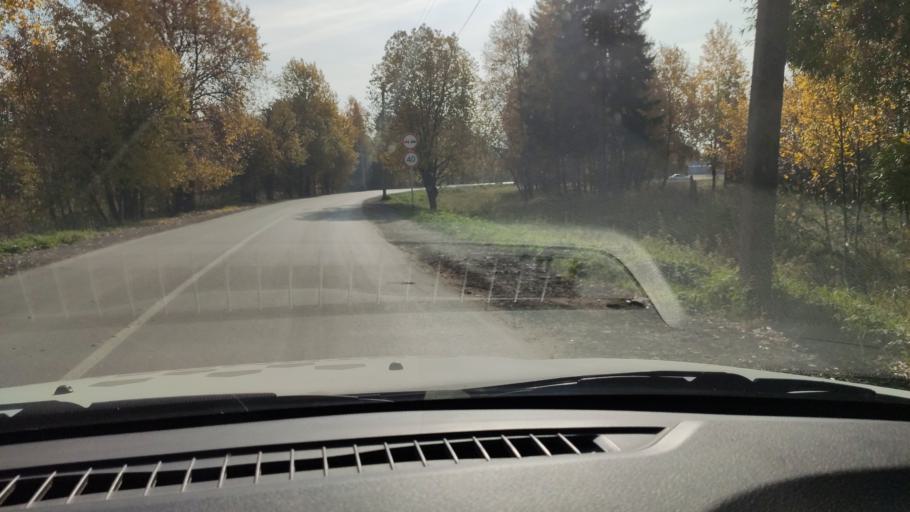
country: RU
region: Perm
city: Sylva
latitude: 58.0325
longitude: 56.7404
